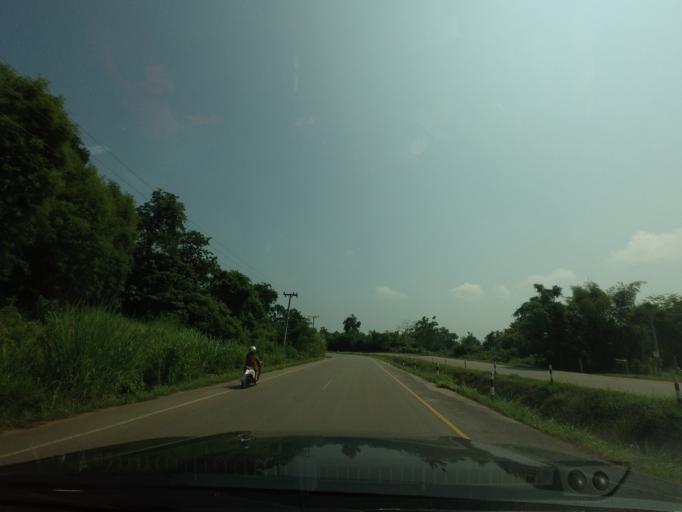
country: TH
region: Nan
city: Nan
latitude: 18.7897
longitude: 100.7523
